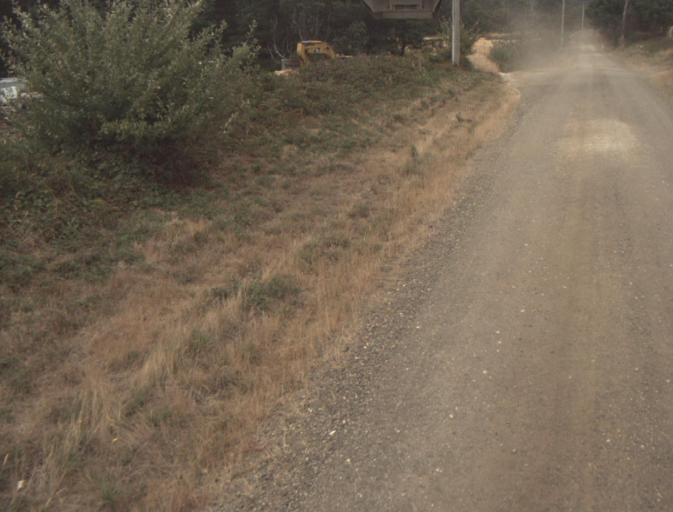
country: AU
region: Tasmania
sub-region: Dorset
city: Bridport
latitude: -41.1835
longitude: 147.2618
